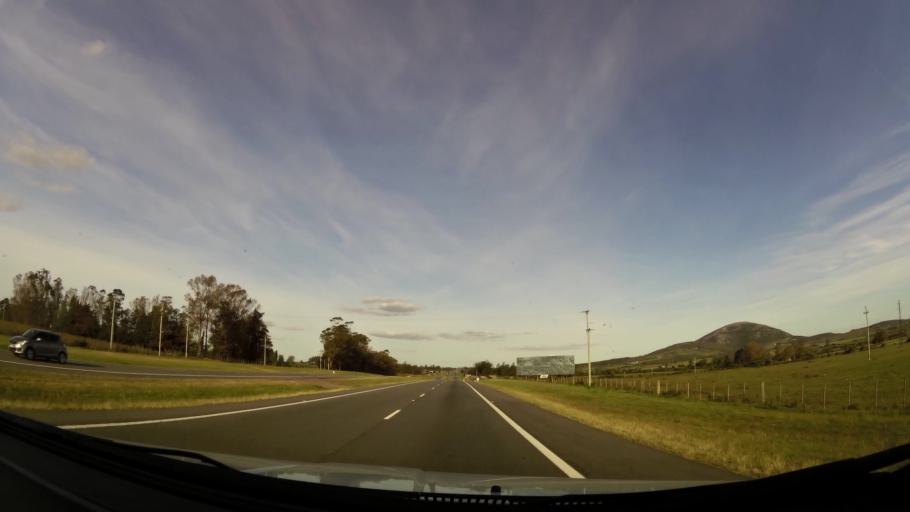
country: UY
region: Maldonado
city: Pan de Azucar
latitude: -34.7904
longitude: -55.3060
